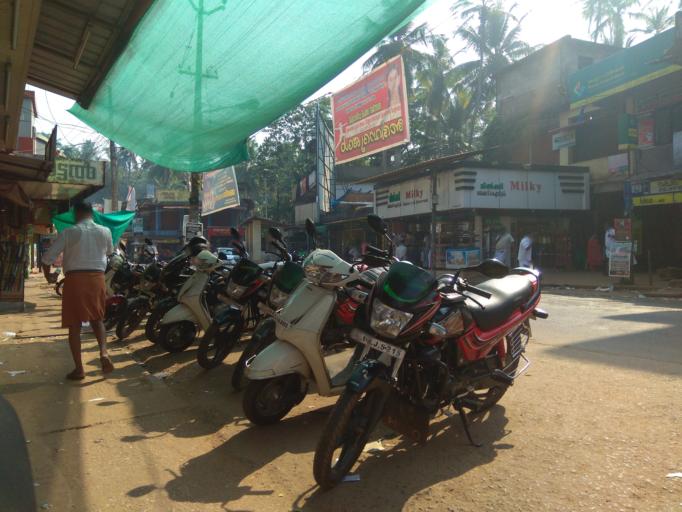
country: IN
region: Kerala
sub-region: Kozhikode
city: Nadapuram
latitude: 11.6570
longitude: 75.6578
